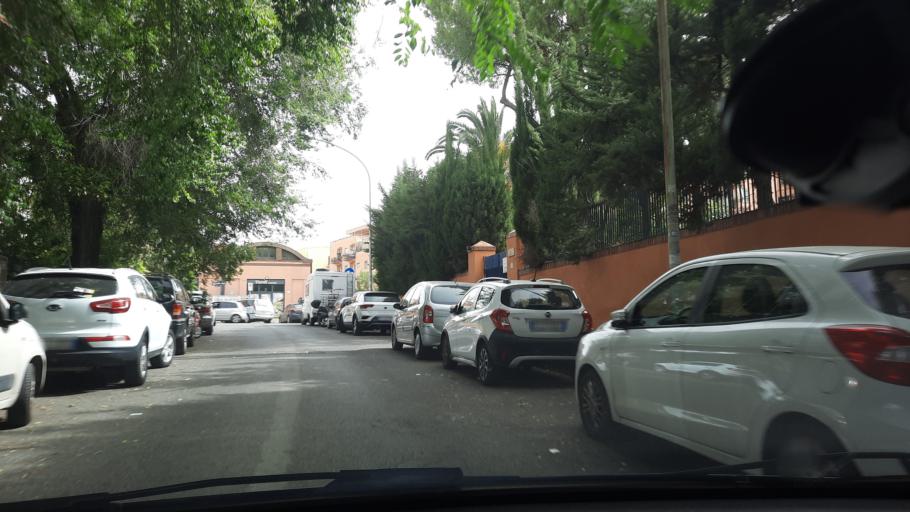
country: IT
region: Latium
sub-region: Citta metropolitana di Roma Capitale
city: Rome
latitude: 41.8611
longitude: 12.4900
